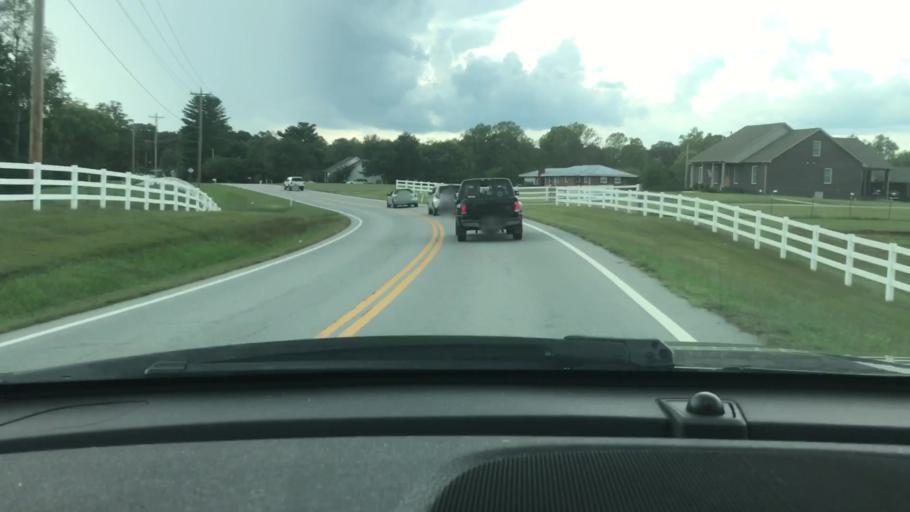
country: US
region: Tennessee
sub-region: Dickson County
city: Charlotte
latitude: 36.2136
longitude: -87.2686
